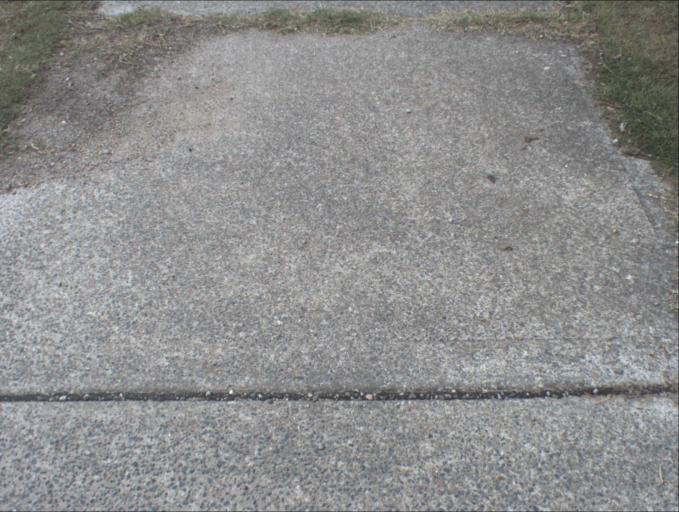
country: AU
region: Queensland
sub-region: Logan
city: Beenleigh
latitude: -27.7091
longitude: 153.2003
